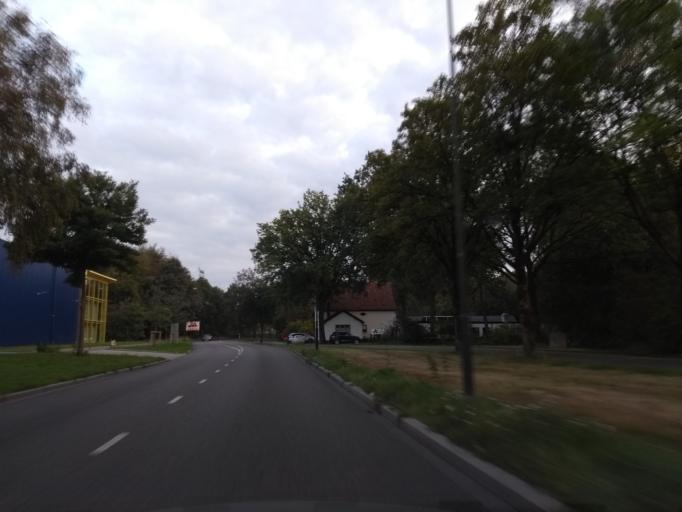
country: NL
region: Gelderland
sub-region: Gemeente Apeldoorn
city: Apeldoorn
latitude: 52.1868
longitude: 5.9818
